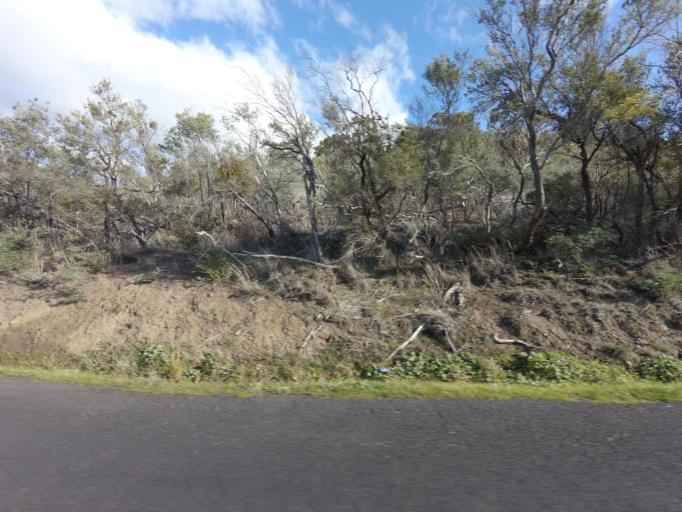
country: AU
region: Tasmania
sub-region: Derwent Valley
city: New Norfolk
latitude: -42.7466
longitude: 147.0427
